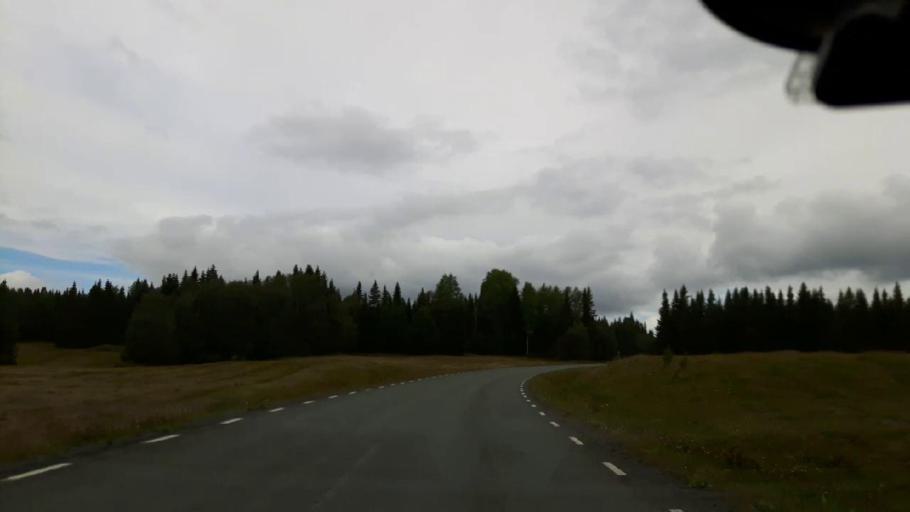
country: SE
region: Jaemtland
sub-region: Krokoms Kommun
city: Valla
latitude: 63.5727
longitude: 13.8334
